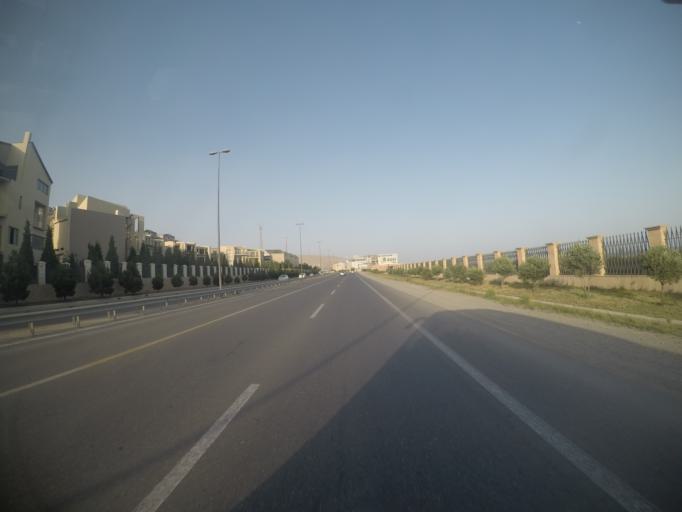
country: AZ
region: Baki
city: Badamdar
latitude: 40.3050
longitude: 49.7871
